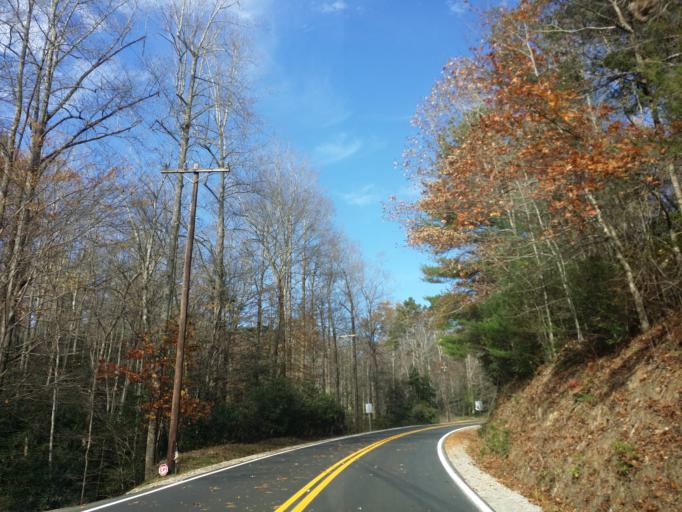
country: US
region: North Carolina
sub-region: McDowell County
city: Marion
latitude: 35.7178
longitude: -82.0766
